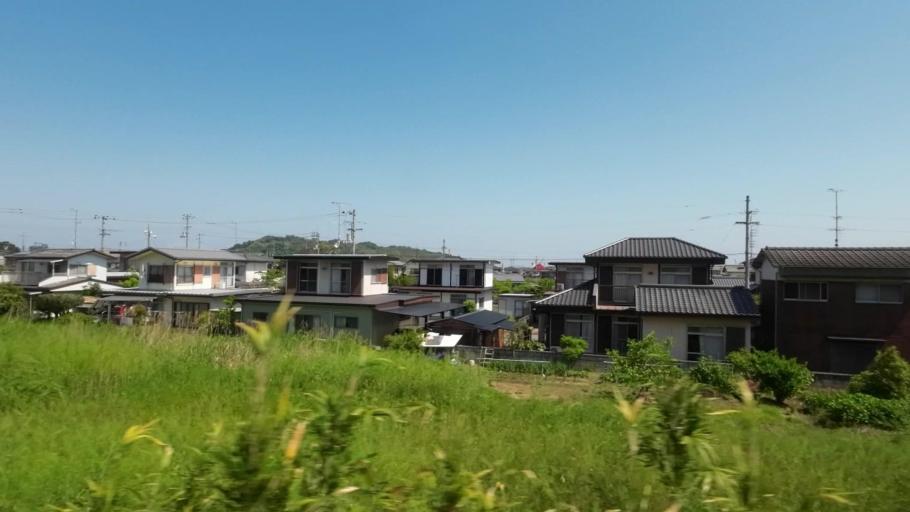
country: JP
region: Ehime
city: Niihama
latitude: 33.9705
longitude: 133.3294
